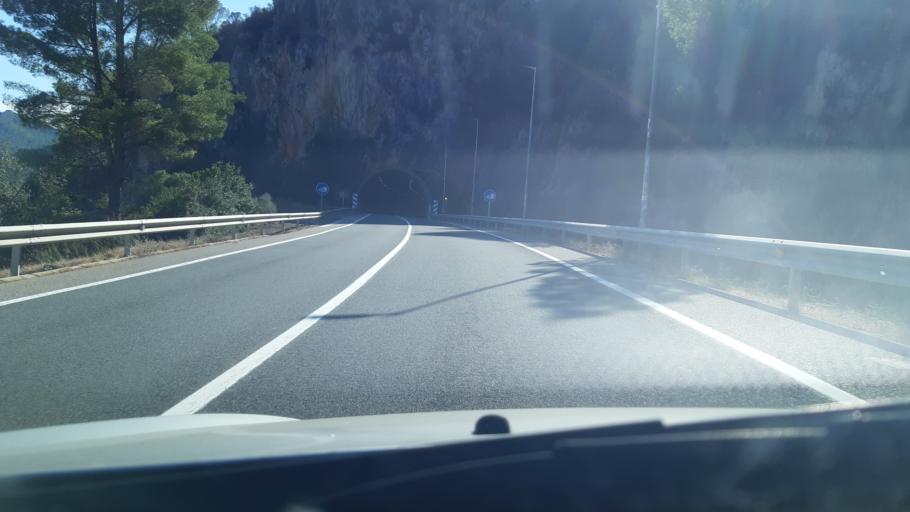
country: ES
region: Catalonia
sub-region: Provincia de Tarragona
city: Benifallet
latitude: 40.9514
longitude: 0.4831
